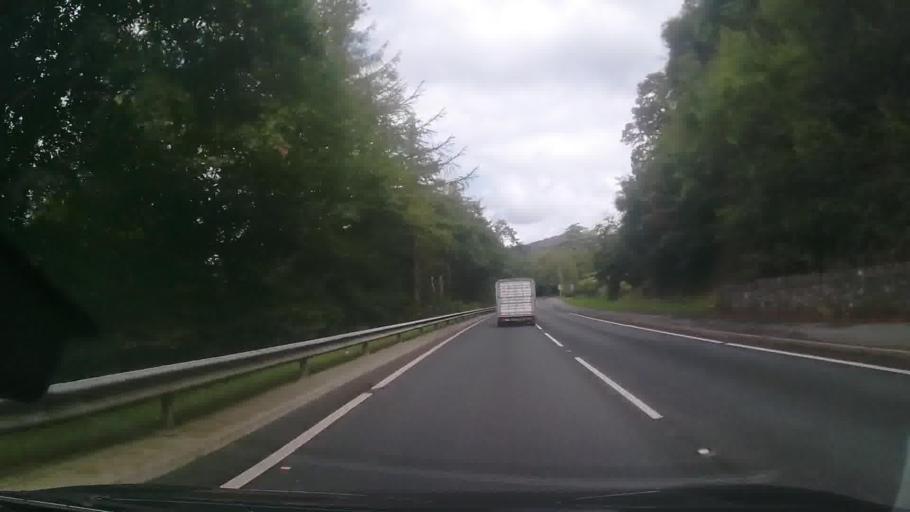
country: GB
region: Wales
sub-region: Gwynedd
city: Dolgellau
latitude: 52.7497
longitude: -3.9050
